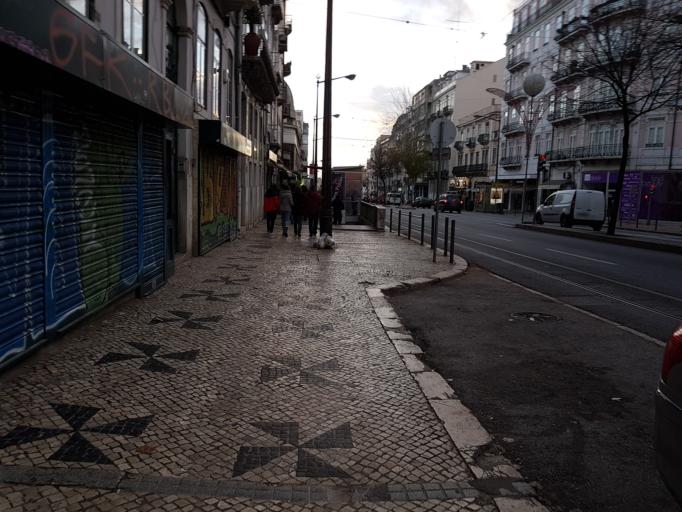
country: PT
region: Lisbon
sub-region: Lisbon
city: Lisbon
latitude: 38.7231
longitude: -9.1351
